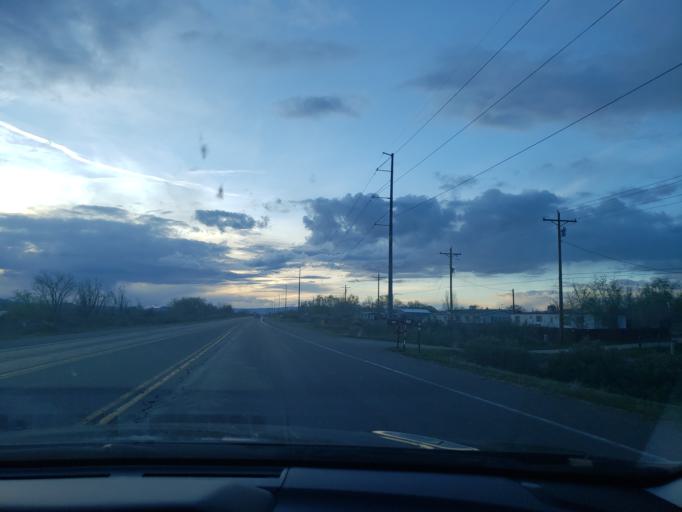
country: US
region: Colorado
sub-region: Mesa County
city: Redlands
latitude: 39.1249
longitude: -108.6735
